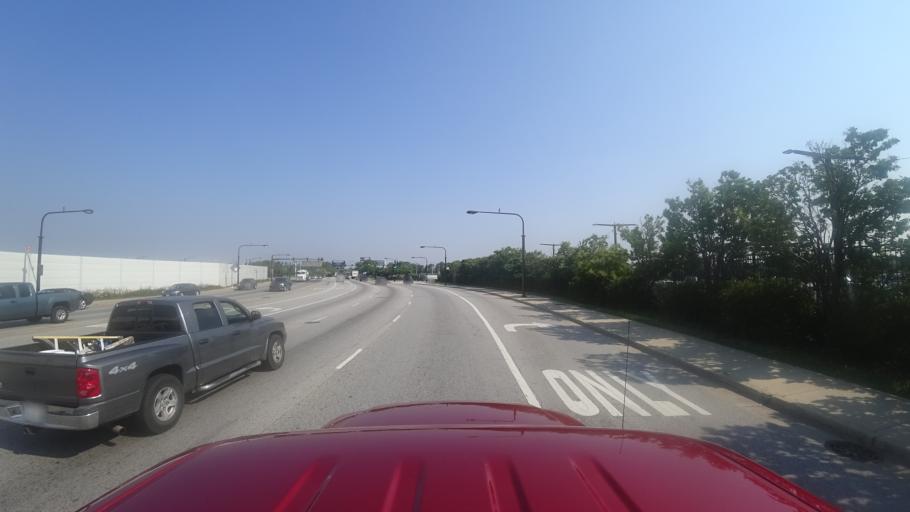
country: US
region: Illinois
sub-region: Cook County
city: Stickney
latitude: 41.7919
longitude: -87.7414
